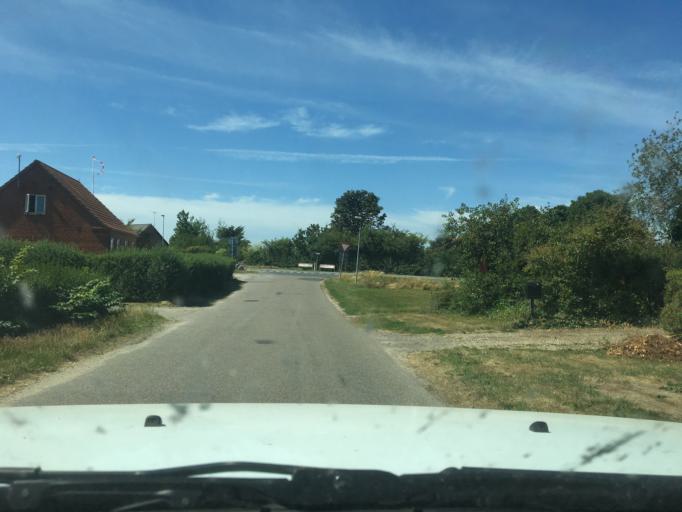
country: DK
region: Central Jutland
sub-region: Viborg Kommune
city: Bjerringbro
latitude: 56.5295
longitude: 9.6609
